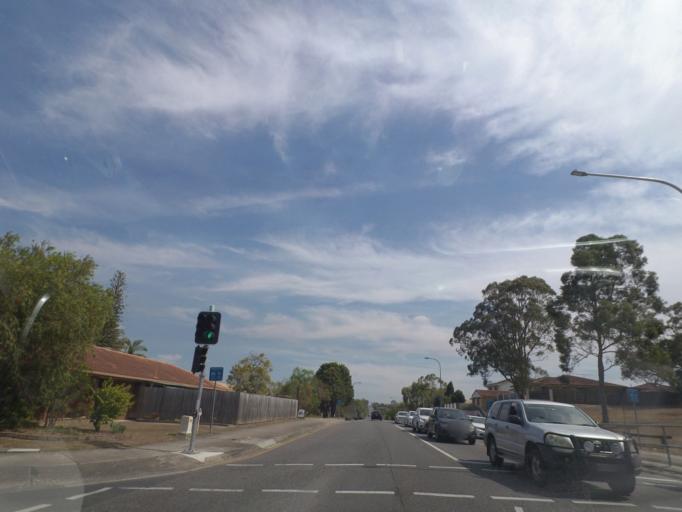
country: AU
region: Queensland
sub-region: Brisbane
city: Sunnybank Hills
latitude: -27.6035
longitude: 153.0635
